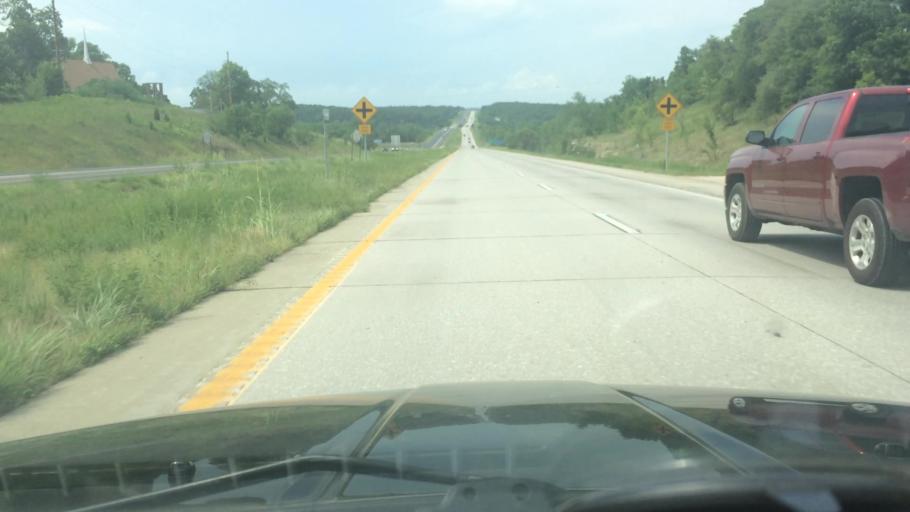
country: US
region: Missouri
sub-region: Saint Clair County
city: Osceola
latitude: 38.0491
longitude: -93.6862
